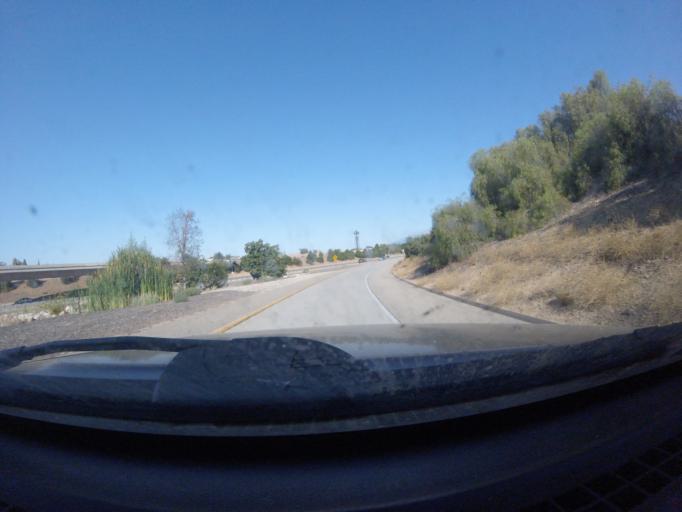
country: US
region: California
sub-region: San Bernardino County
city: Highland
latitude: 34.1305
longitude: -117.2043
